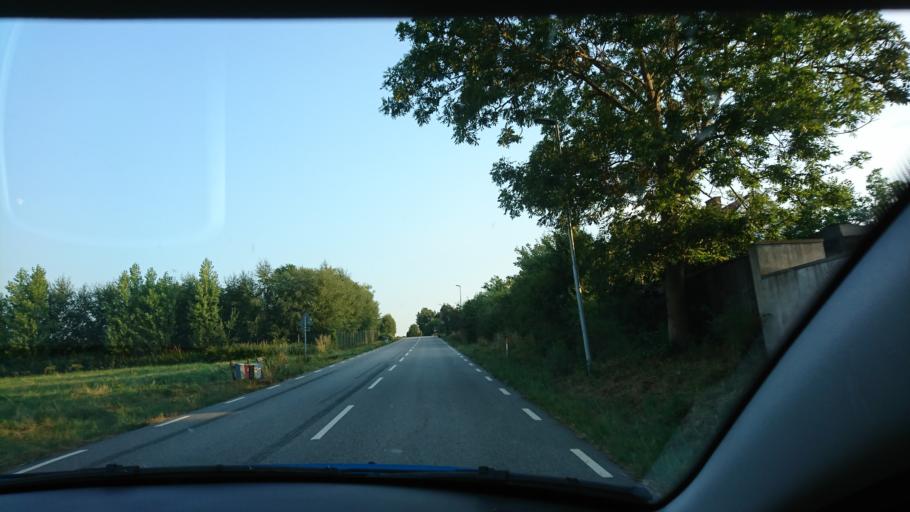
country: SE
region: Skane
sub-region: Simrishamns Kommun
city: Kivik
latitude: 55.7072
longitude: 14.1514
